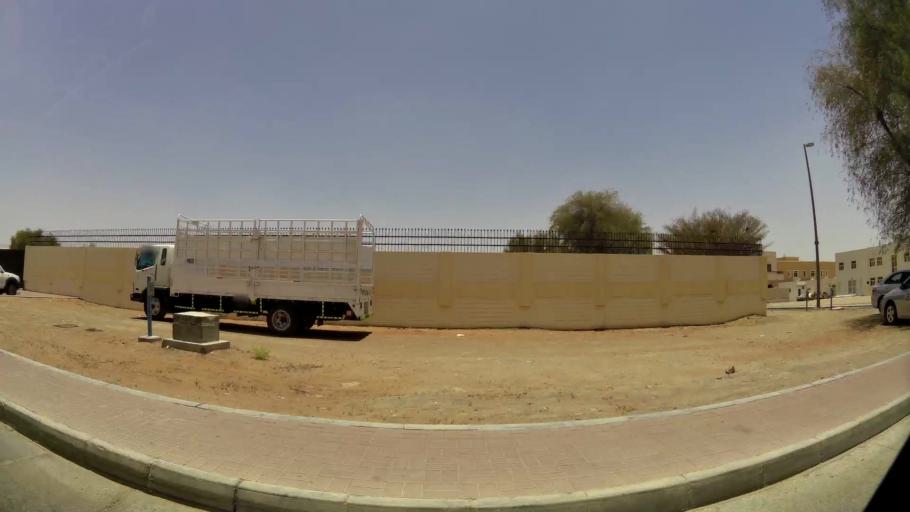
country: OM
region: Al Buraimi
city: Al Buraymi
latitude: 24.2614
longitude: 55.7364
